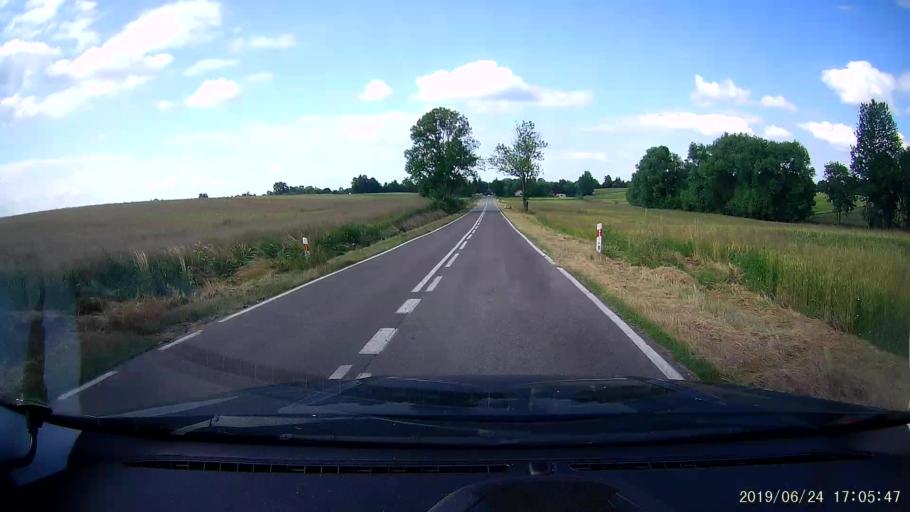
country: PL
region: Lublin Voivodeship
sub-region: Powiat hrubieszowski
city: Dolhobyczow
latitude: 50.5797
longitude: 23.9672
